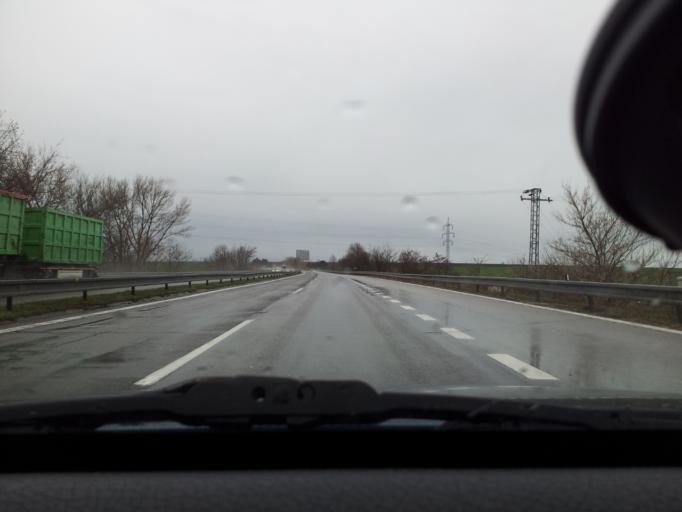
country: SK
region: Nitriansky
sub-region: Okres Nitra
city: Nitra
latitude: 48.3237
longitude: 17.9397
